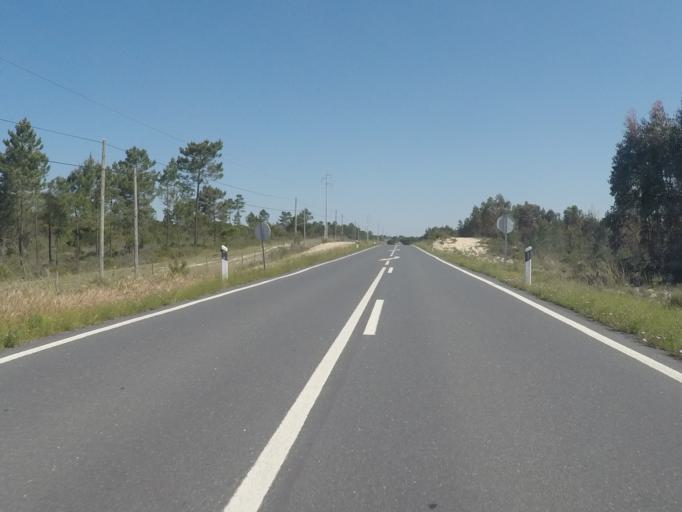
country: PT
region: Setubal
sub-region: Grandola
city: Grandola
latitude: 38.2434
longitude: -8.7374
